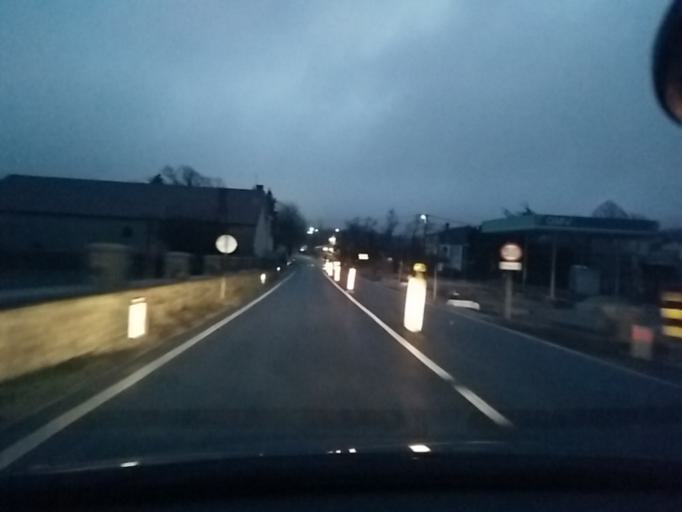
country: SI
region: Hrpelje-Kozina
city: Kozina
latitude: 45.6186
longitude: 13.9103
